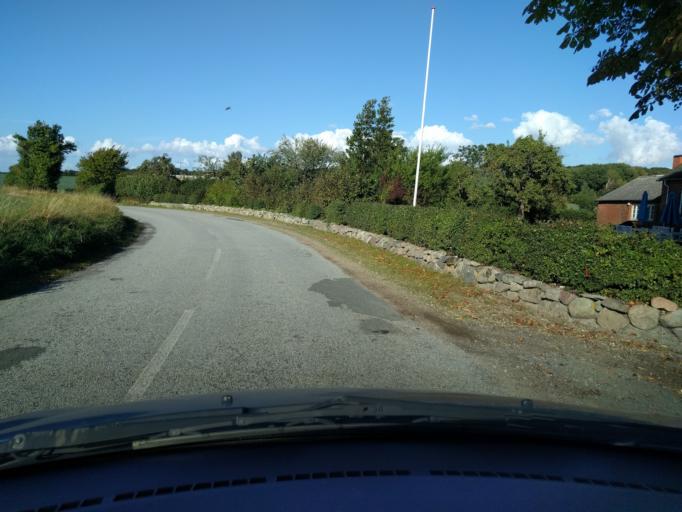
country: DK
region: South Denmark
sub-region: Assens Kommune
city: Harby
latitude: 55.1362
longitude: 10.0267
